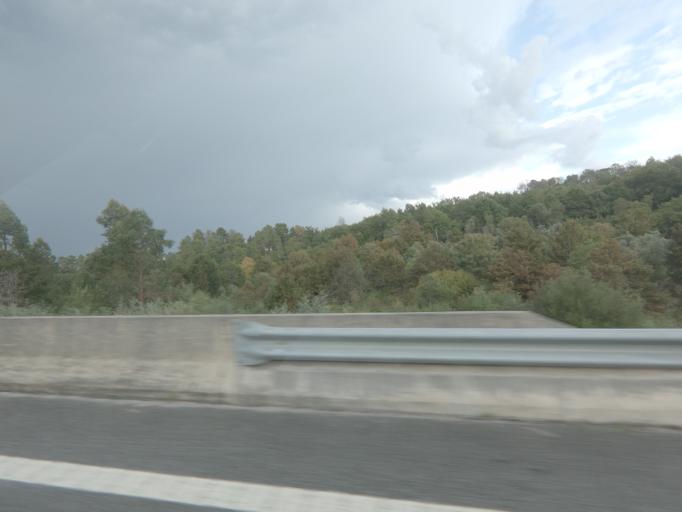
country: PT
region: Viseu
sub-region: Viseu
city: Abraveses
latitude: 40.6538
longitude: -7.9665
